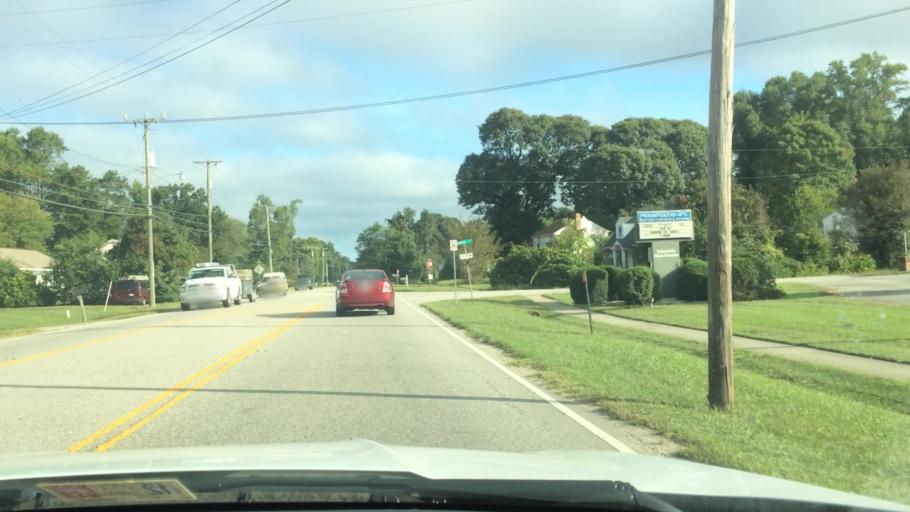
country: US
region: Virginia
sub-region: City of Williamsburg
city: Williamsburg
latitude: 37.2222
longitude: -76.6259
